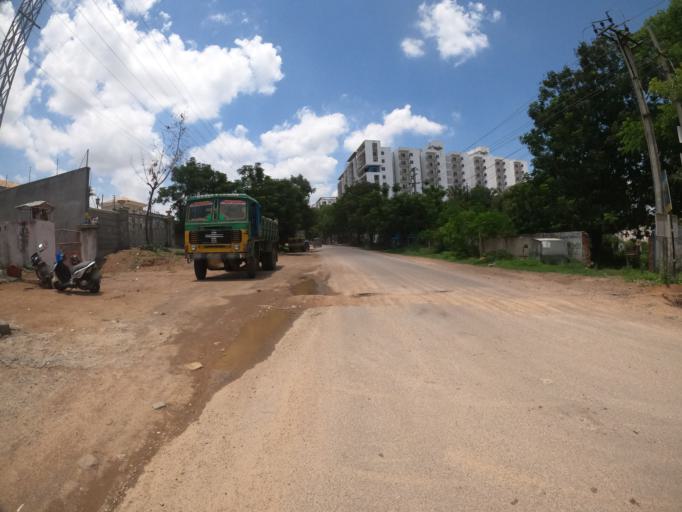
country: IN
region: Telangana
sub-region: Medak
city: Serilingampalle
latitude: 17.3844
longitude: 78.3260
